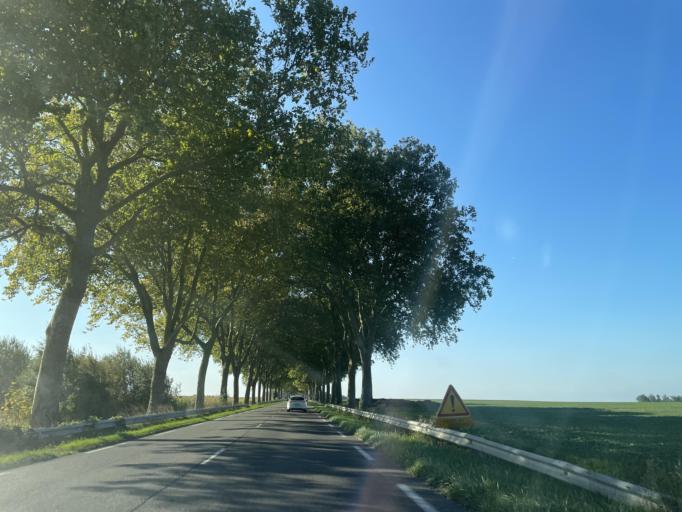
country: FR
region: Ile-de-France
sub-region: Departement de Seine-et-Marne
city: Guerard
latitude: 48.8384
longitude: 2.9736
